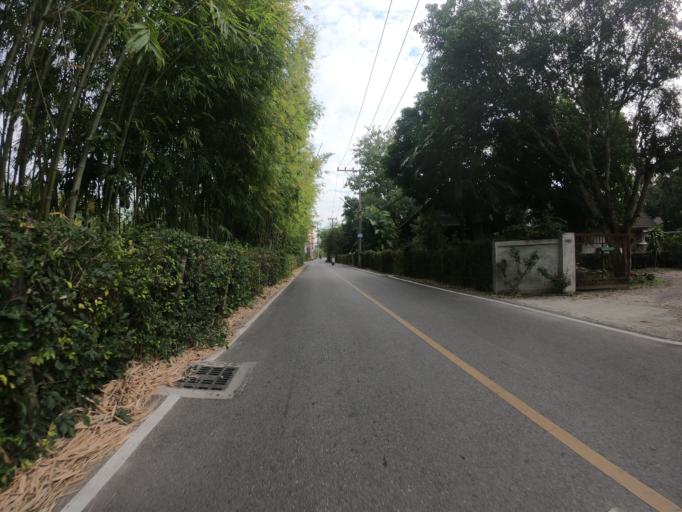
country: TH
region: Chiang Mai
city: Chiang Mai
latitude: 18.8150
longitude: 98.9655
